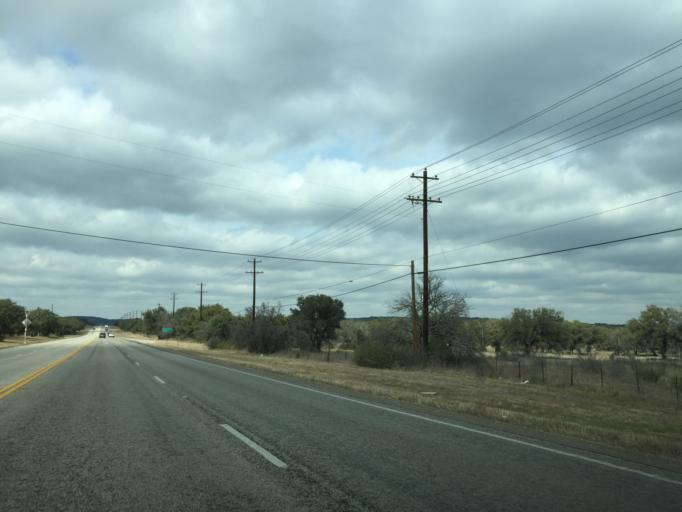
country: US
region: Texas
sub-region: Travis County
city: Briarcliff
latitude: 30.4102
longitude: -98.1097
